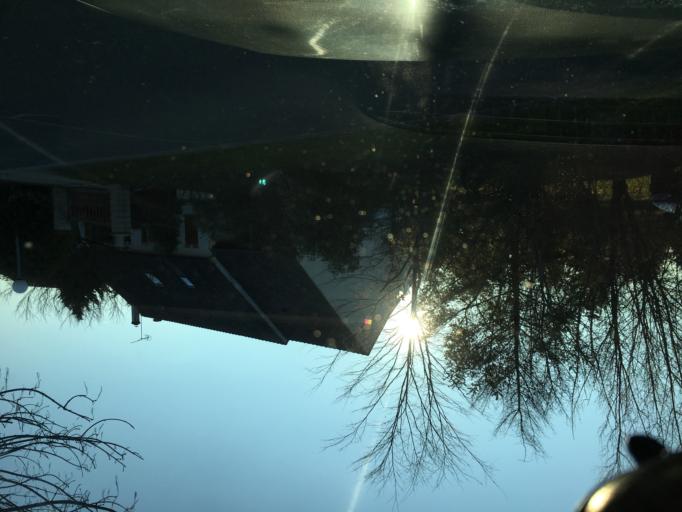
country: FR
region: Centre
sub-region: Departement du Loiret
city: Jouy-le-Potier
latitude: 47.7800
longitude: 1.8772
